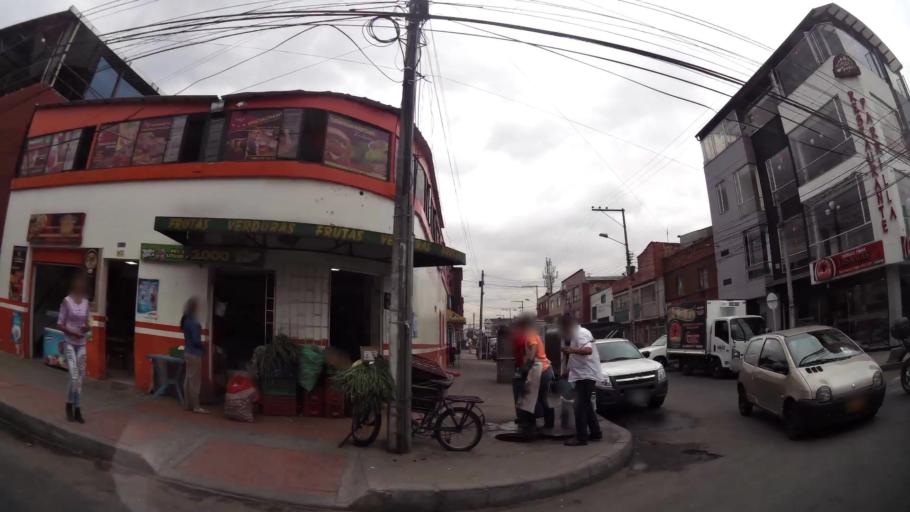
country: CO
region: Bogota D.C.
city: Barrio San Luis
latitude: 4.6704
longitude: -74.0675
